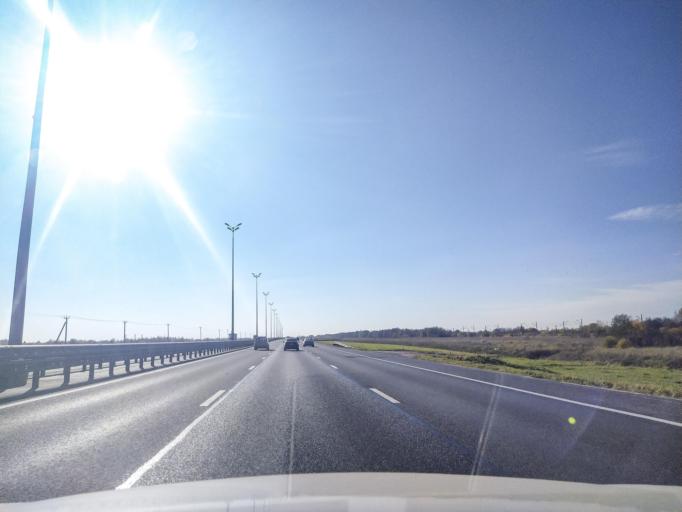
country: RU
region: Leningrad
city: Maloye Verevo
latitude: 59.6332
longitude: 30.2119
